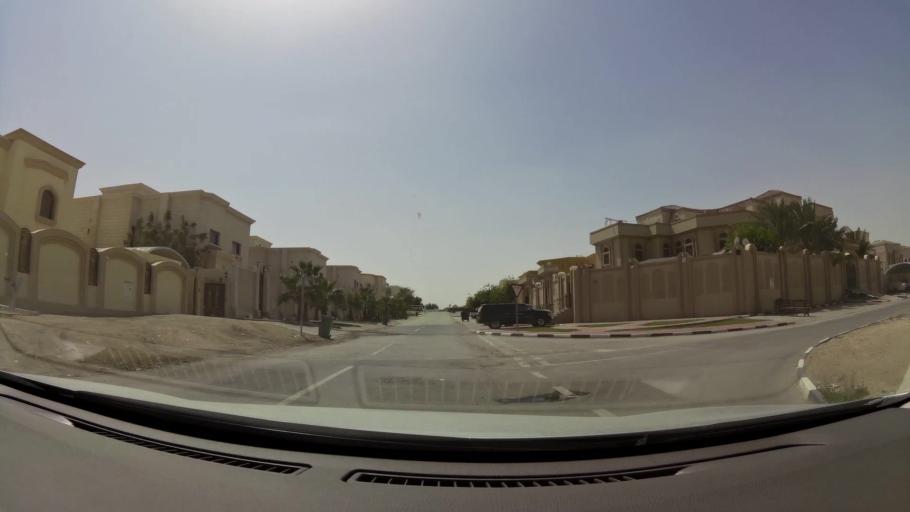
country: QA
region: Baladiyat Umm Salal
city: Umm Salal Muhammad
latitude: 25.3840
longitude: 51.4214
